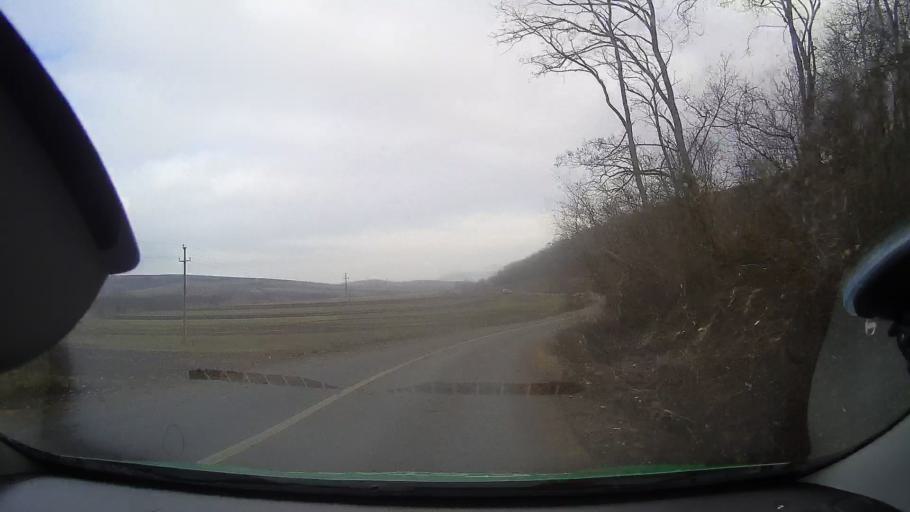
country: RO
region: Mures
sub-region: Comuna Ludus
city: Gheja
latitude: 46.4068
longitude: 24.0667
